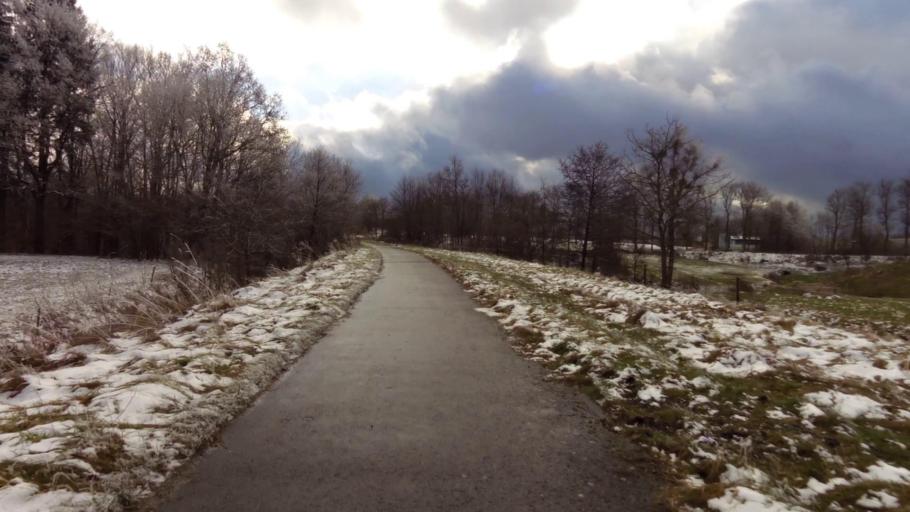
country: PL
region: West Pomeranian Voivodeship
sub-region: Powiat swidwinski
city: Polczyn-Zdroj
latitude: 53.7333
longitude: 16.0428
